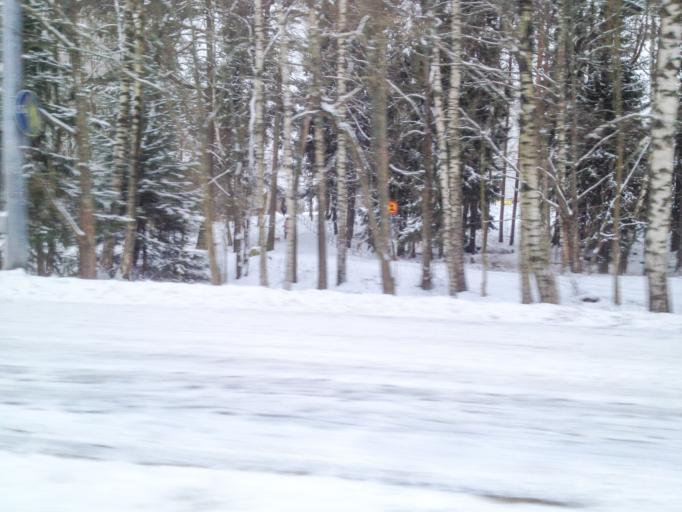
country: FI
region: Uusimaa
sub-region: Helsinki
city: Vantaa
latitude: 60.2156
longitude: 25.1332
